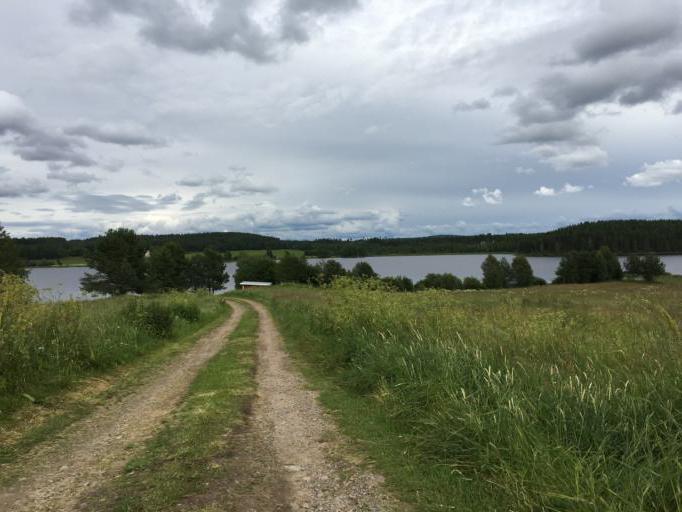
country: SE
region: Norrbotten
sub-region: Overkalix Kommun
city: OEverkalix
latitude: 66.1097
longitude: 22.7884
